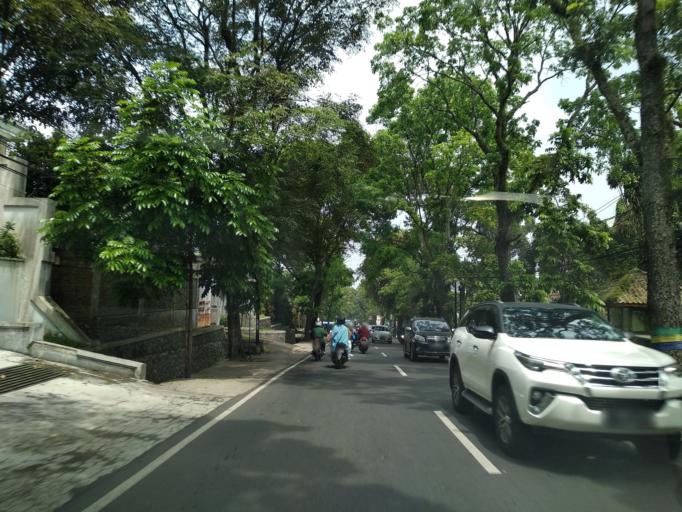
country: ID
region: West Java
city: Lembang
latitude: -6.8532
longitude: 107.5963
